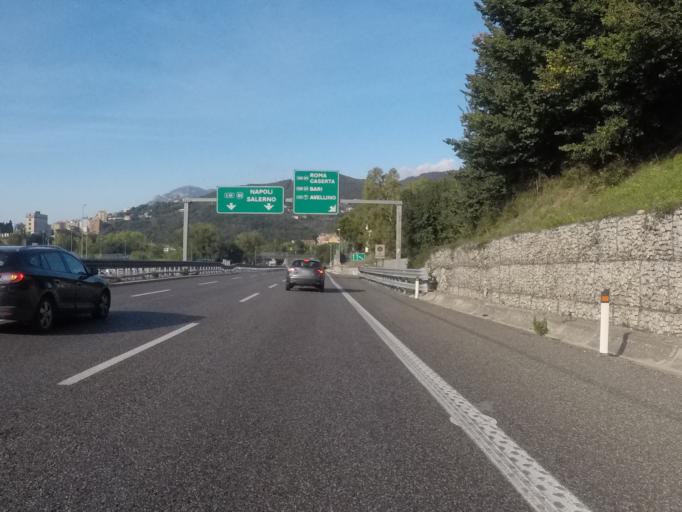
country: IT
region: Campania
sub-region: Provincia di Salerno
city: Capezzano Inferiore
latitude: 40.6971
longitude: 14.7867
